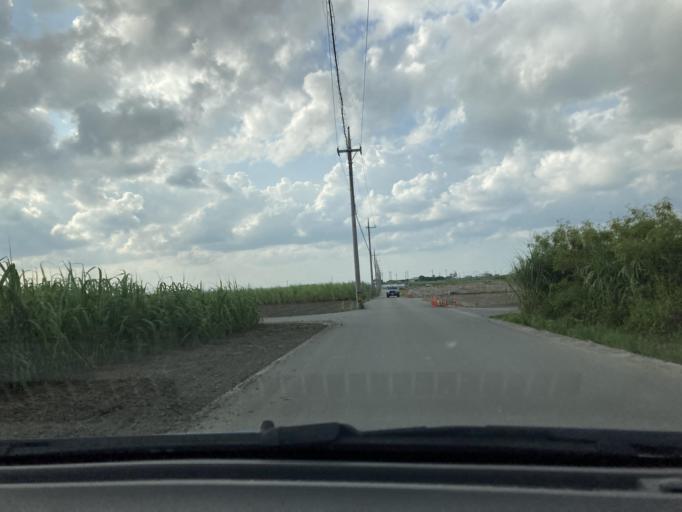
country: JP
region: Okinawa
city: Itoman
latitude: 26.0821
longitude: 127.6691
